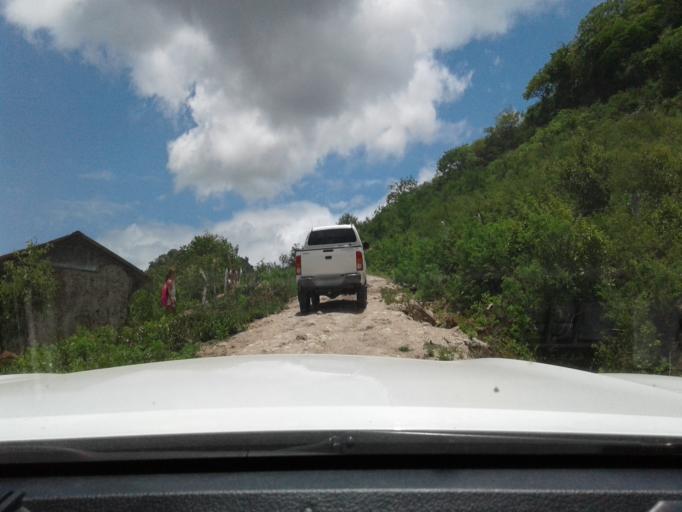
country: NI
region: Matagalpa
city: Ciudad Dario
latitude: 12.6776
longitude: -86.1404
